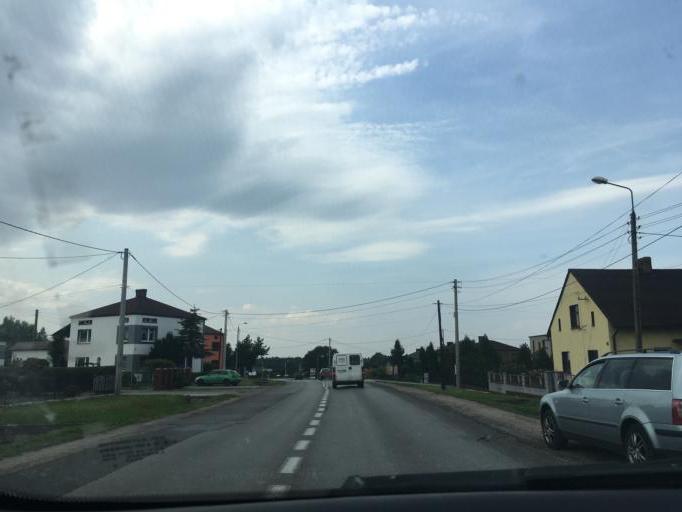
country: PL
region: Silesian Voivodeship
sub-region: Powiat raciborski
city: Pogrzebien
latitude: 50.0746
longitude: 18.3079
